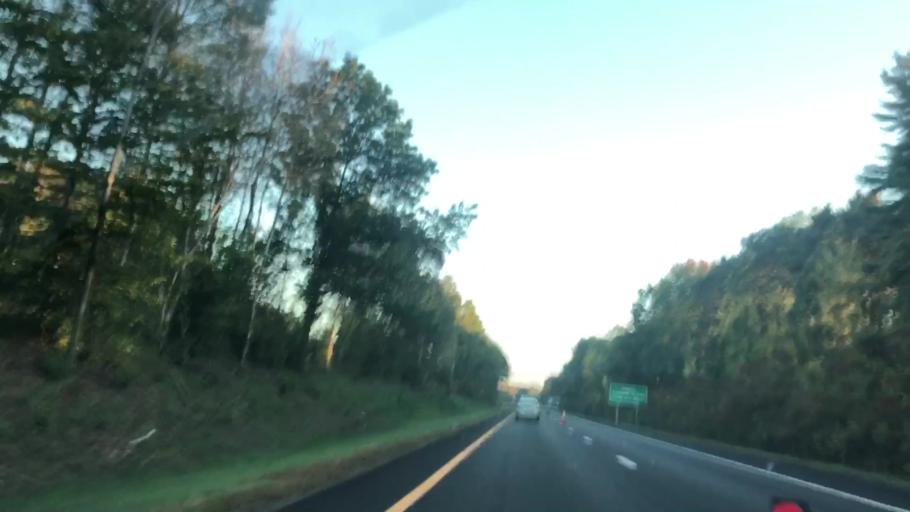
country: US
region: Massachusetts
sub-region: Franklin County
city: South Deerfield
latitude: 42.4996
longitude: -72.6187
